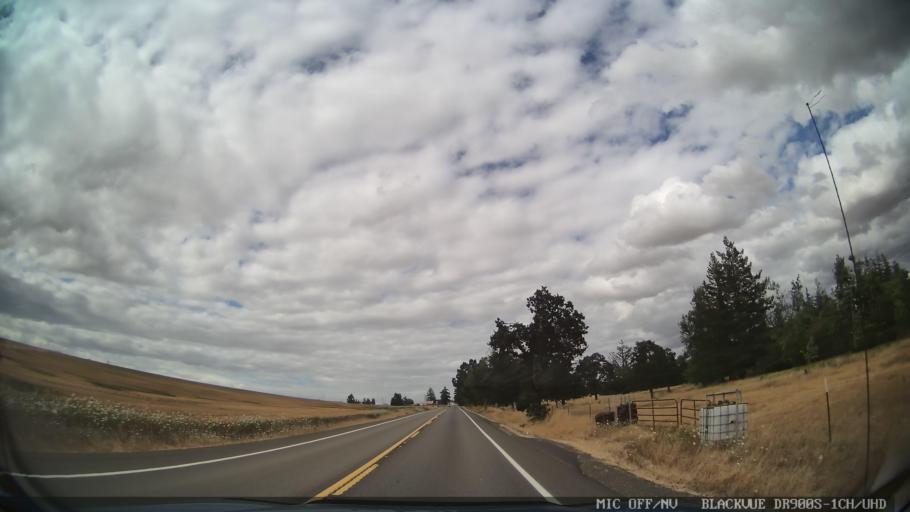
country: US
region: Oregon
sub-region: Marion County
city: Sublimity
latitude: 44.8542
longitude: -122.7932
